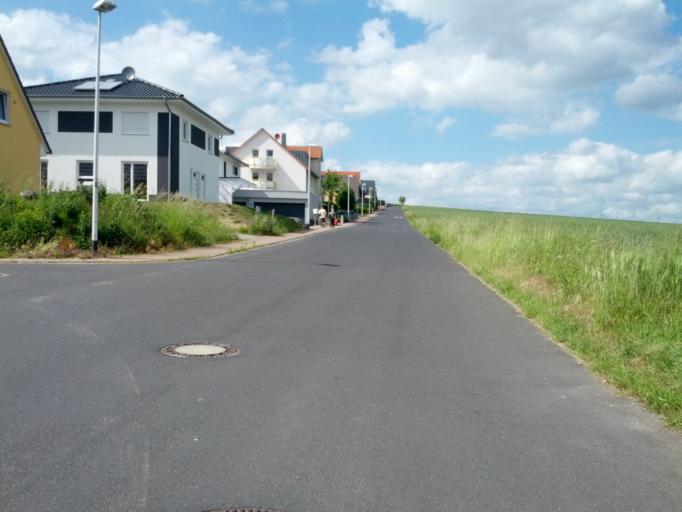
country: DE
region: Thuringia
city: Eisenach
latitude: 51.0058
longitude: 10.3111
